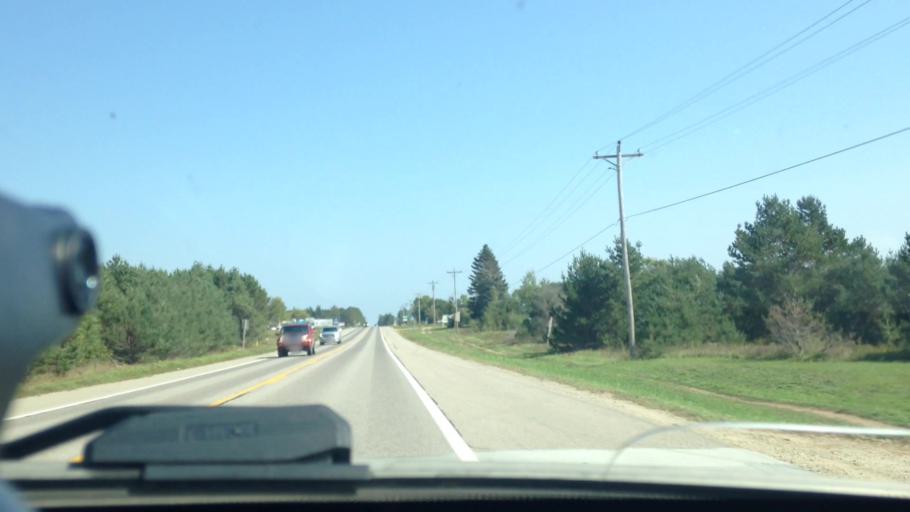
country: US
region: Michigan
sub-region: Luce County
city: Newberry
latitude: 46.3038
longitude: -85.4978
